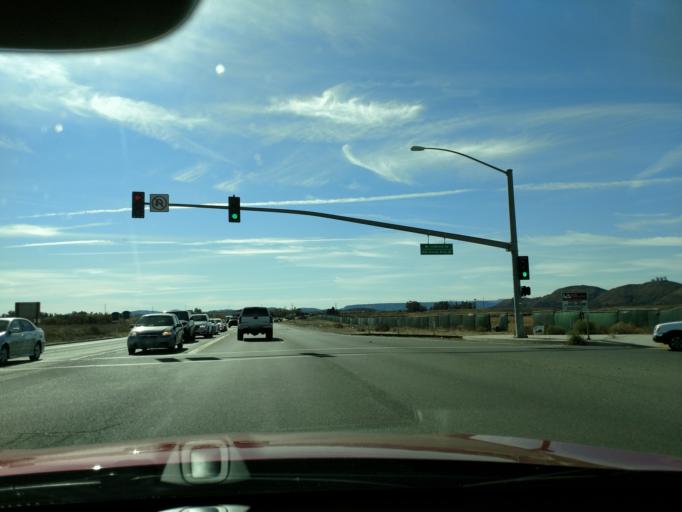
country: US
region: California
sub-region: Riverside County
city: Murrieta Hot Springs
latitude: 33.5981
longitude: -117.1185
